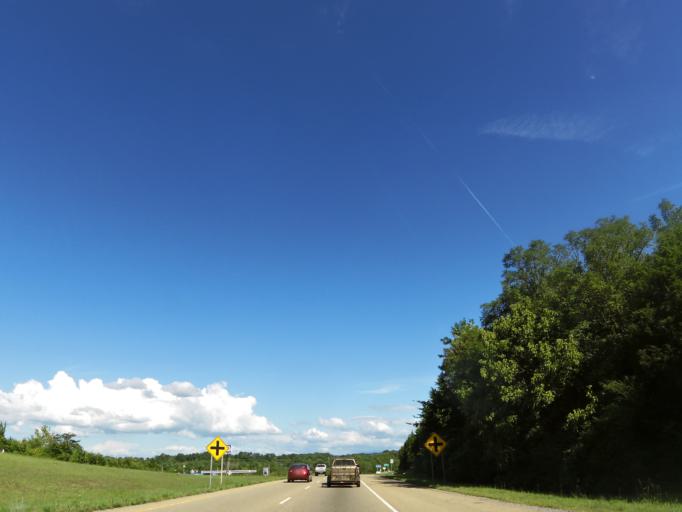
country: US
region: Tennessee
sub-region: Greene County
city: Mosheim
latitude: 36.2224
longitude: -83.0323
